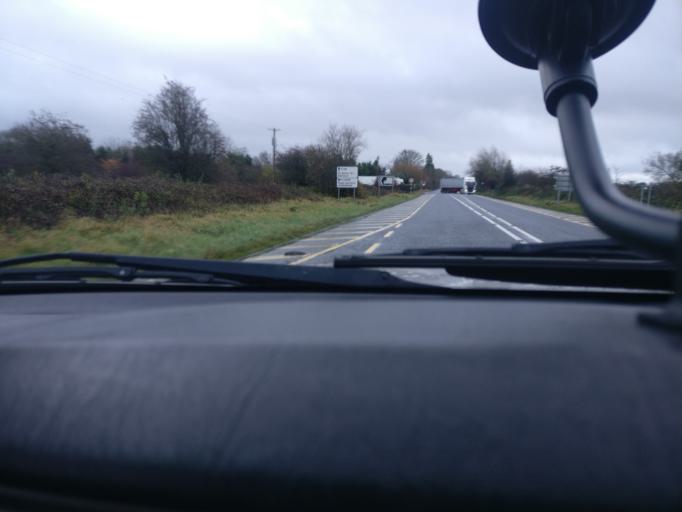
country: IE
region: Leinster
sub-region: An Mhi
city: Longwood
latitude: 53.4258
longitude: -6.8926
